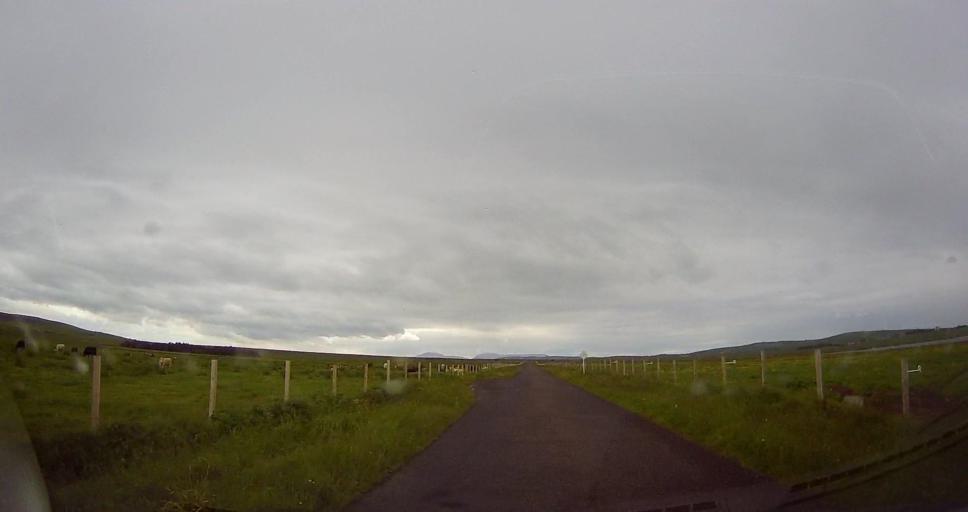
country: GB
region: Scotland
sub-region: Orkney Islands
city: Stromness
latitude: 59.1083
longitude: -3.2541
